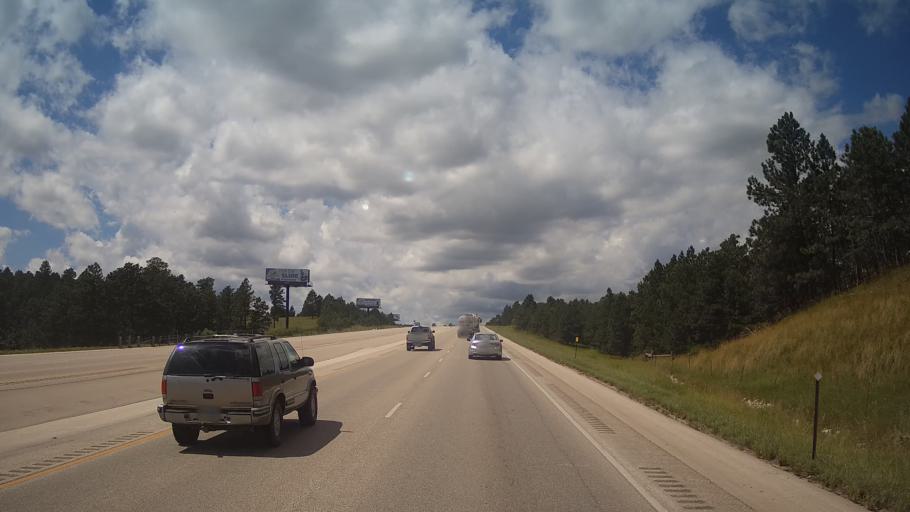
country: US
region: South Dakota
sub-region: Pennington County
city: Colonial Pine Hills
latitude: 43.9732
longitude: -103.2867
